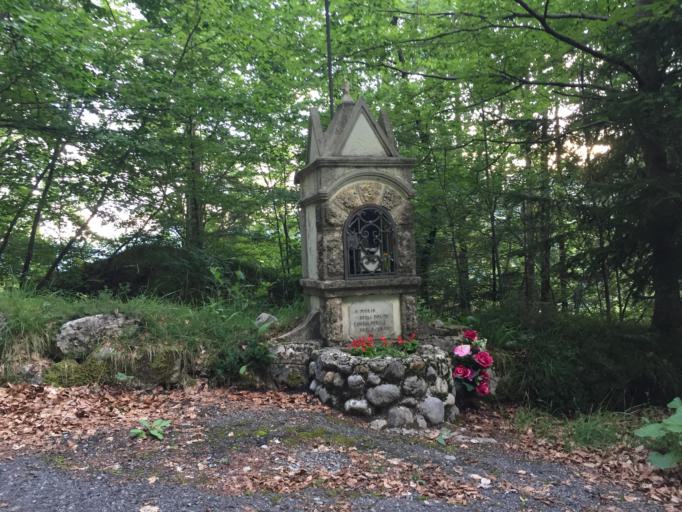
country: IT
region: Friuli Venezia Giulia
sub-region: Provincia di Udine
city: Paularo
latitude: 46.4771
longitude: 13.0977
